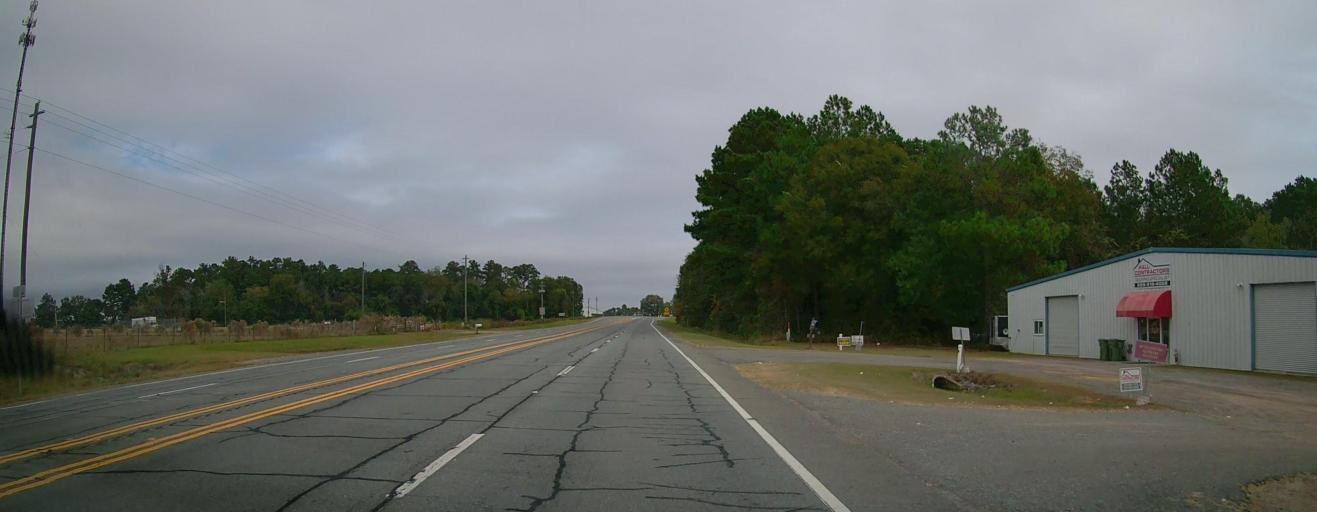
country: US
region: Georgia
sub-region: Tift County
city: Omega
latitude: 31.3270
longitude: -83.6183
